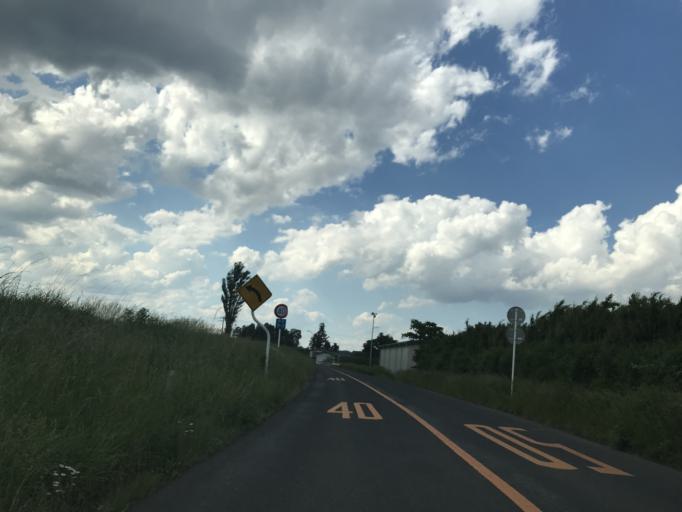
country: JP
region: Miyagi
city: Wakuya
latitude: 38.6682
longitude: 141.2124
